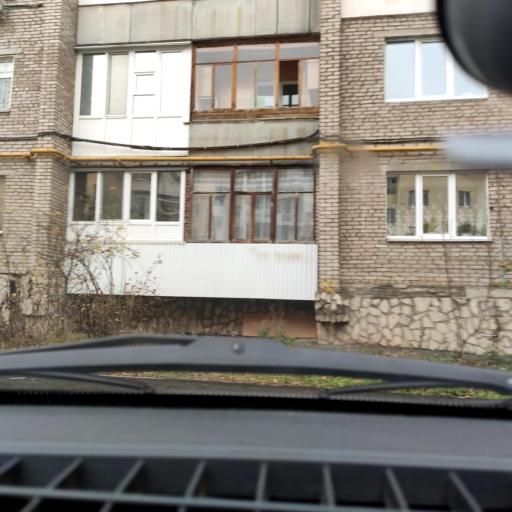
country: RU
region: Bashkortostan
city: Ufa
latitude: 54.7436
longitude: 55.9583
